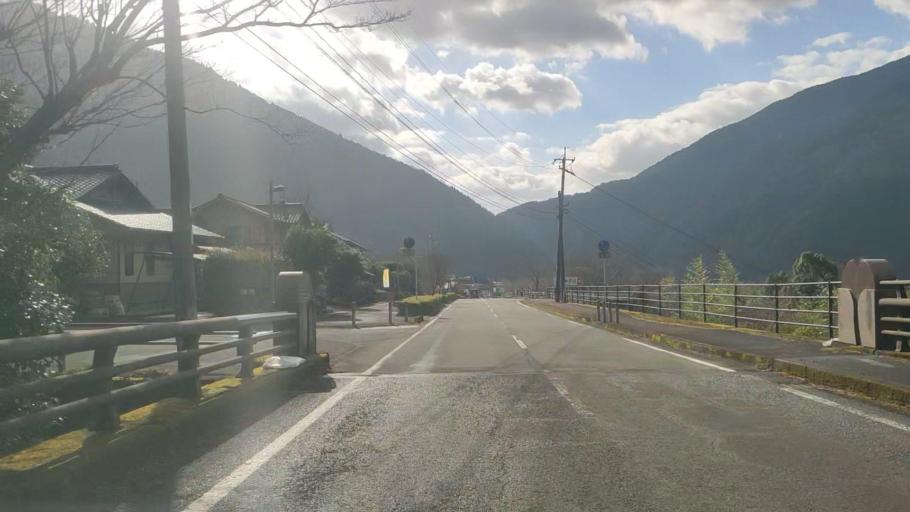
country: JP
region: Kumamoto
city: Hitoyoshi
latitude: 32.4029
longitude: 130.8258
